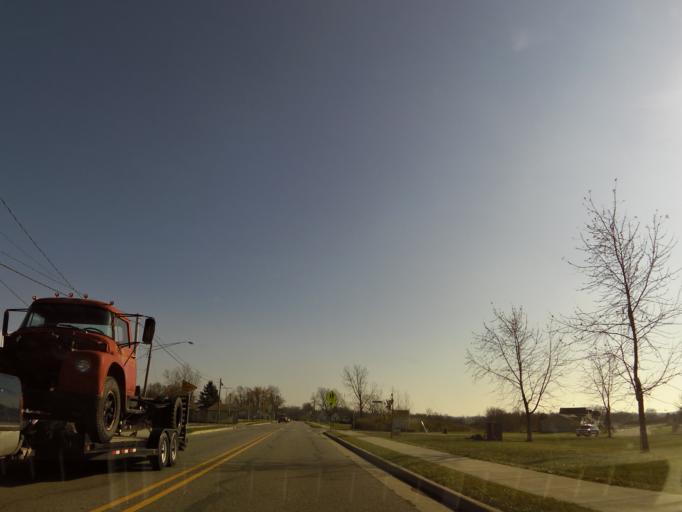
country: US
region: Indiana
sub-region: Union County
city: Liberty
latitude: 39.6324
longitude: -84.9215
